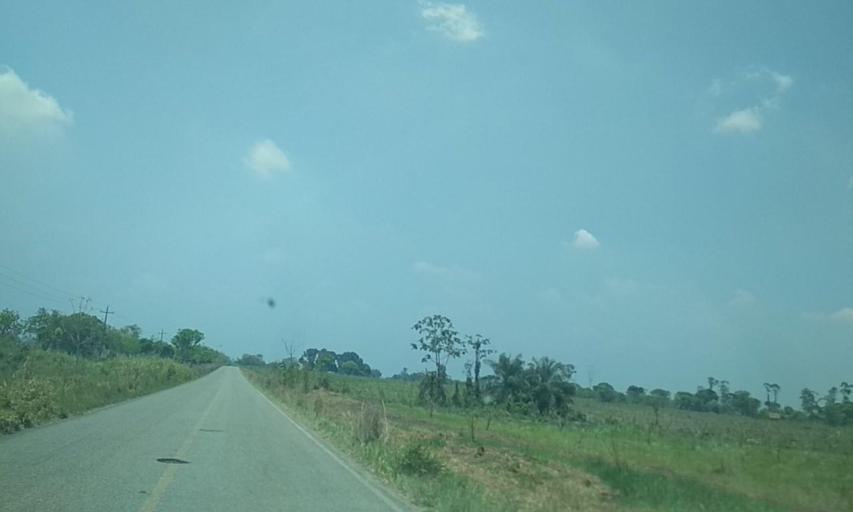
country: MX
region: Tabasco
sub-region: Huimanguillo
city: Paso de la Mina 3ra. Seccion
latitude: 17.8316
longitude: -93.6167
